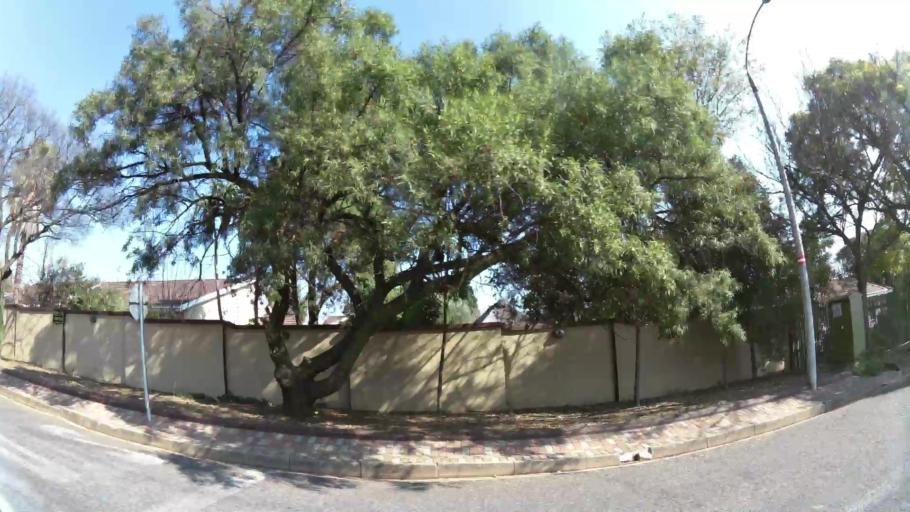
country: ZA
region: Gauteng
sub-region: Ekurhuleni Metropolitan Municipality
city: Boksburg
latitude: -26.2448
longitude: 28.2511
